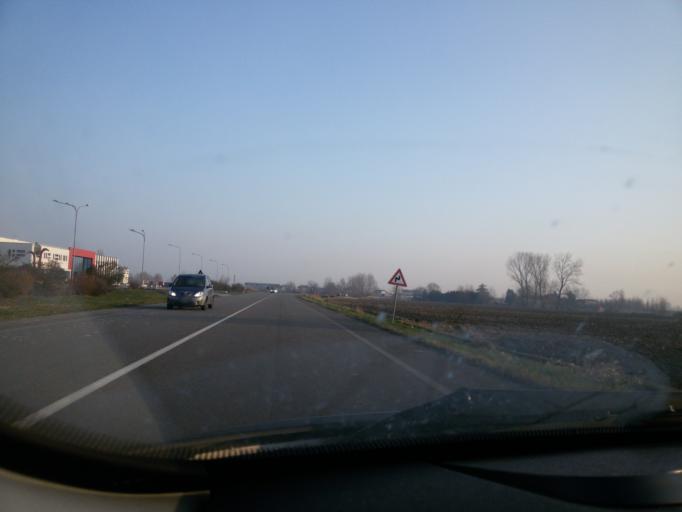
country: IT
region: Piedmont
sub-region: Provincia di Vercelli
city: Stroppiana
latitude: 45.2534
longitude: 8.4612
